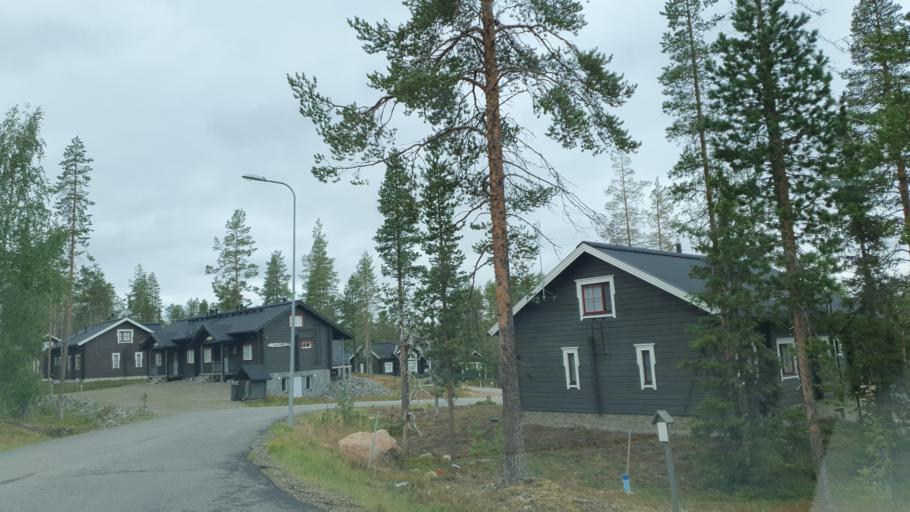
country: FI
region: Lapland
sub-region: Tunturi-Lappi
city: Kolari
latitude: 67.5933
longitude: 24.1803
